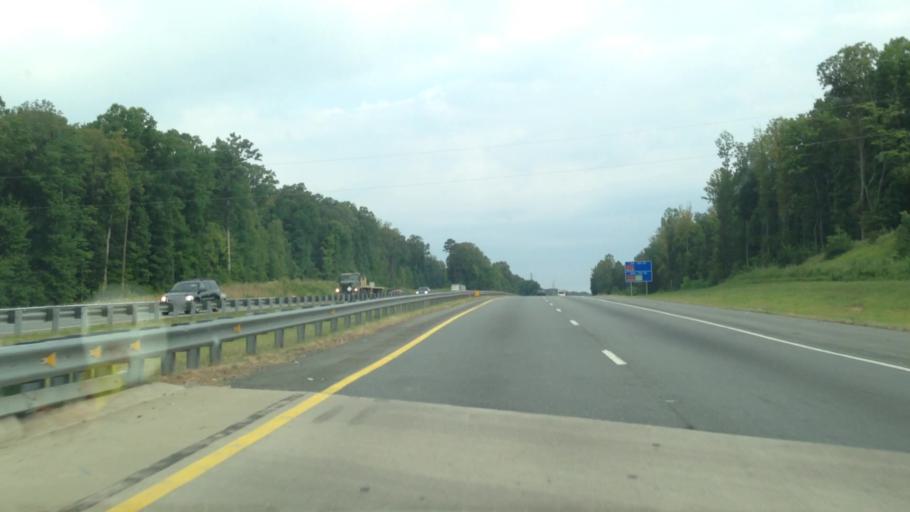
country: US
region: North Carolina
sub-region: Forsyth County
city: Tobaccoville
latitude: 36.2408
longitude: -80.3450
